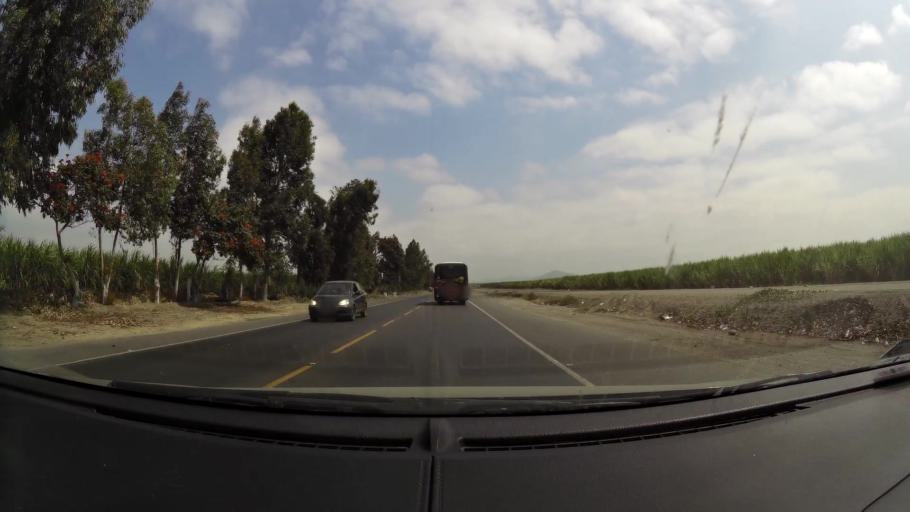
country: PE
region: La Libertad
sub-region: Ascope
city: Chicama
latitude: -7.8387
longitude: -79.1532
